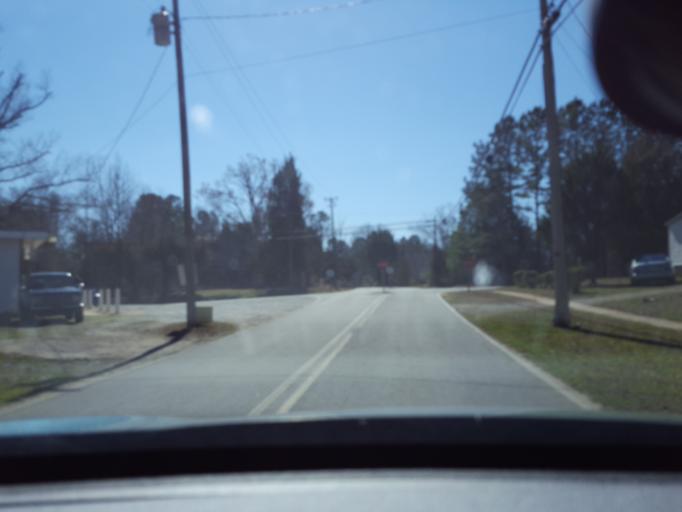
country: US
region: North Carolina
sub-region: Halifax County
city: South Rosemary
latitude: 36.4271
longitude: -77.9110
